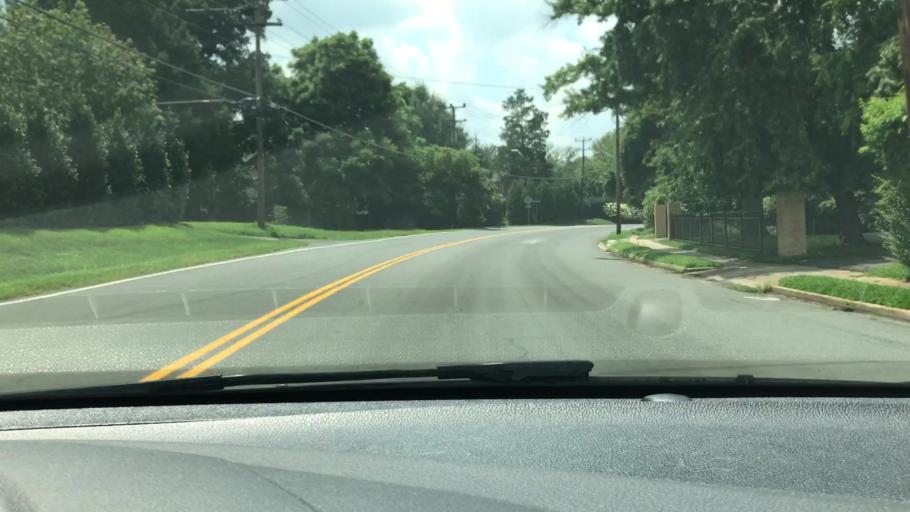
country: US
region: Virginia
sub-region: Fairfax County
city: McLean
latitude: 38.9151
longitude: -77.1613
